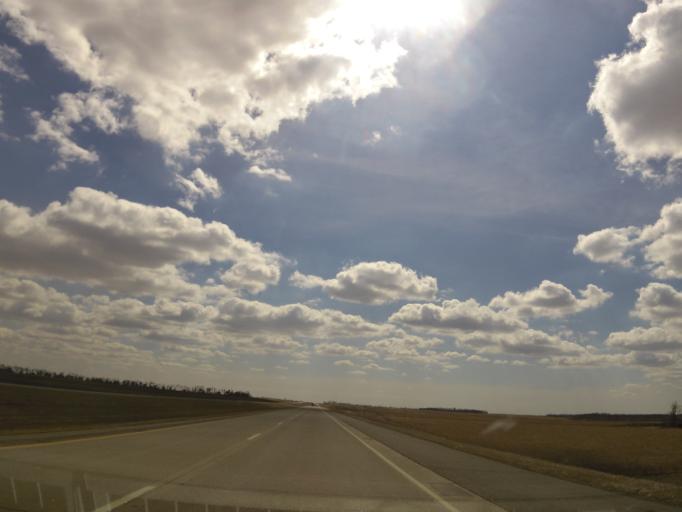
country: US
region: South Dakota
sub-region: Codington County
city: Watertown
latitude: 45.1897
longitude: -97.0570
